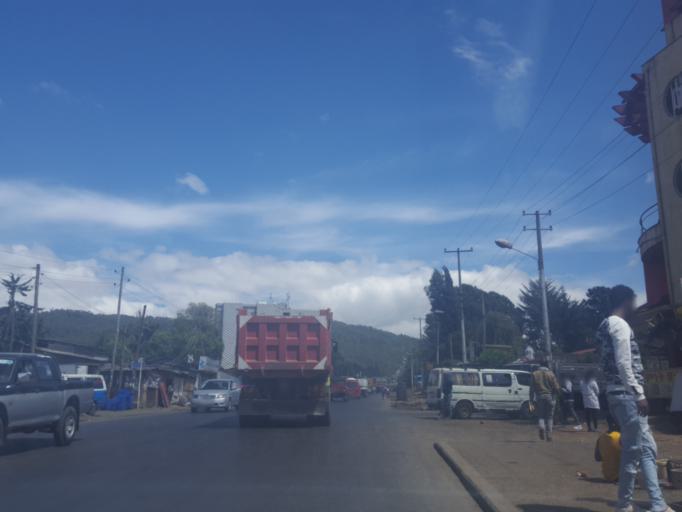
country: ET
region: Adis Abeba
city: Addis Ababa
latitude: 9.0661
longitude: 38.7334
